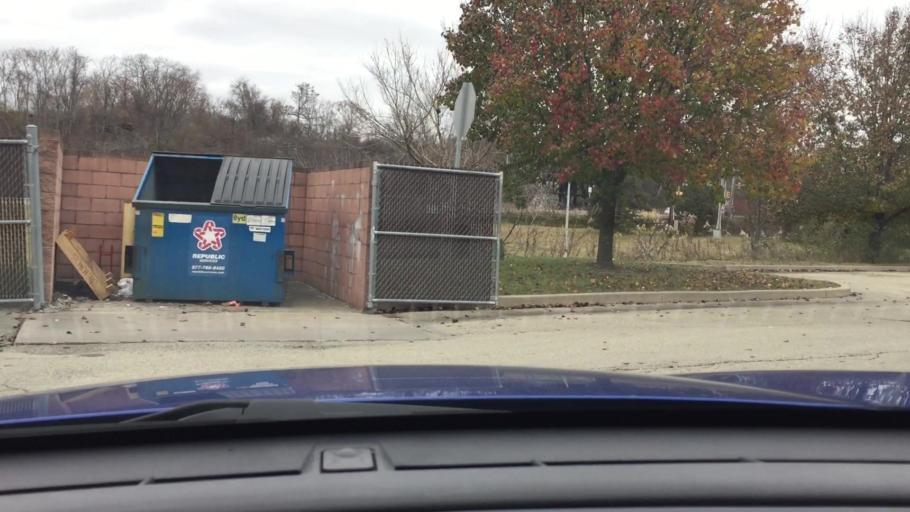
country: US
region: Pennsylvania
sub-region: Westmoreland County
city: Lynnwood-Pricedale
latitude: 40.1398
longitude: -79.8432
